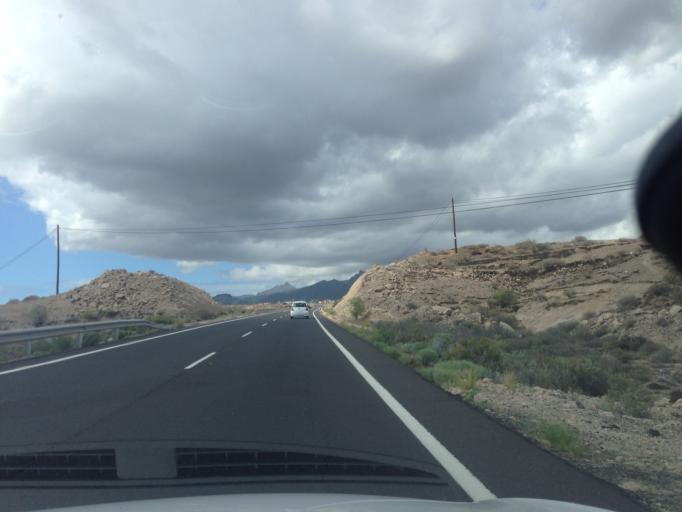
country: ES
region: Canary Islands
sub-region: Provincia de Santa Cruz de Tenerife
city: San Isidro
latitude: 28.0327
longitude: -16.5967
